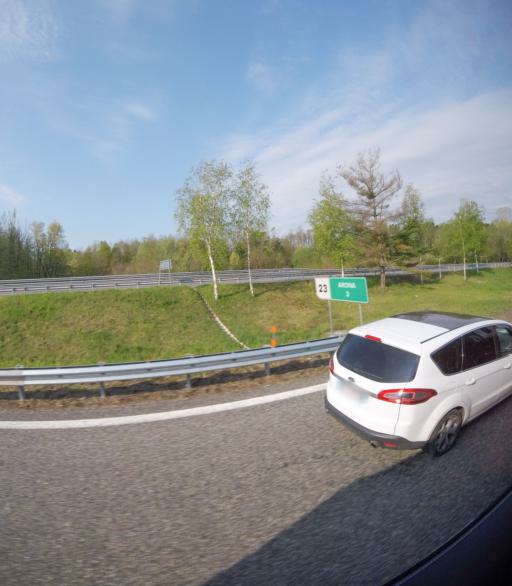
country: IT
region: Piedmont
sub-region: Provincia di Novara
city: Comignago
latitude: 45.7096
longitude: 8.5445
